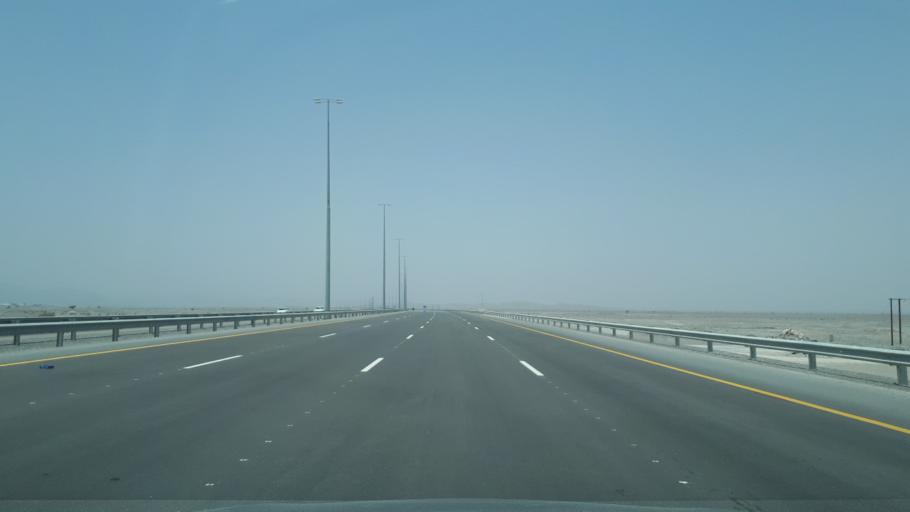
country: OM
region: Al Batinah
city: Barka'
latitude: 23.5651
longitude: 57.7031
